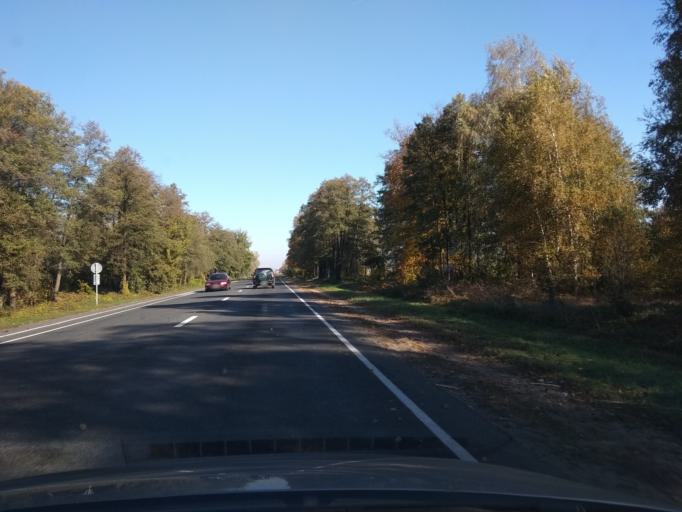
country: BY
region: Brest
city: Kobryn
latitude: 52.1678
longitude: 24.3160
